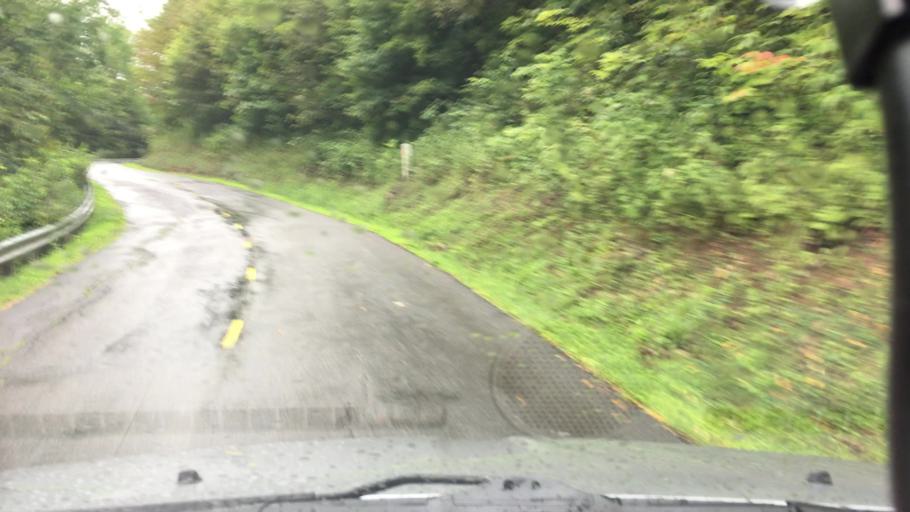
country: US
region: North Carolina
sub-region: Madison County
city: Mars Hill
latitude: 35.9424
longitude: -82.5141
